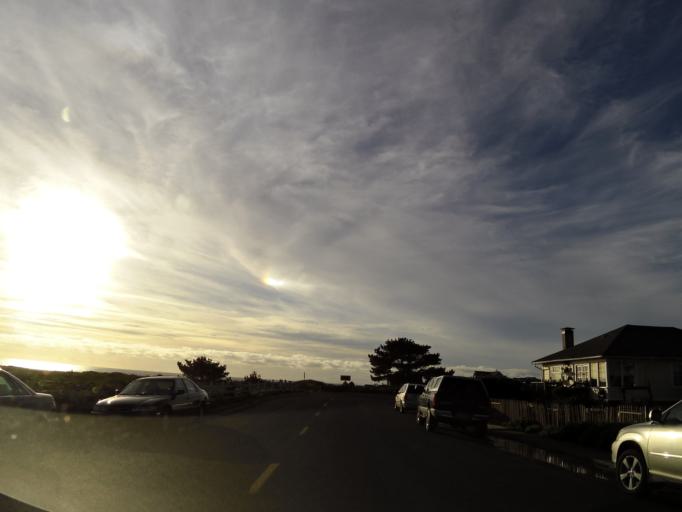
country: US
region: California
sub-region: Mendocino County
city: Fort Bragg
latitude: 39.3042
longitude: -123.8037
